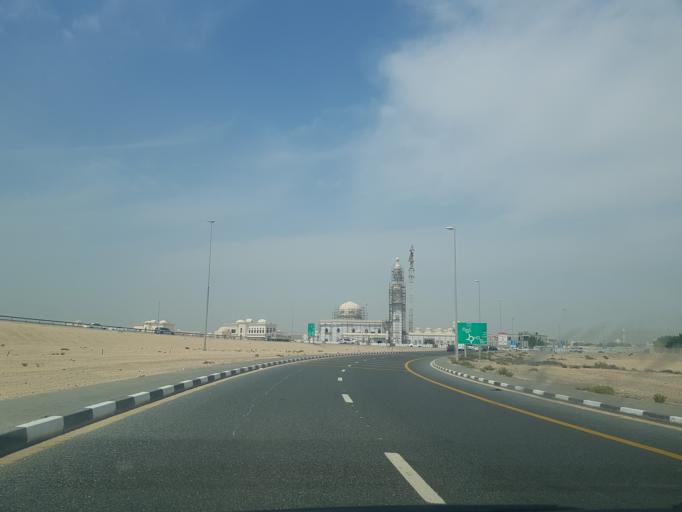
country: AE
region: Ash Shariqah
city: Sharjah
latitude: 25.2693
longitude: 55.4861
